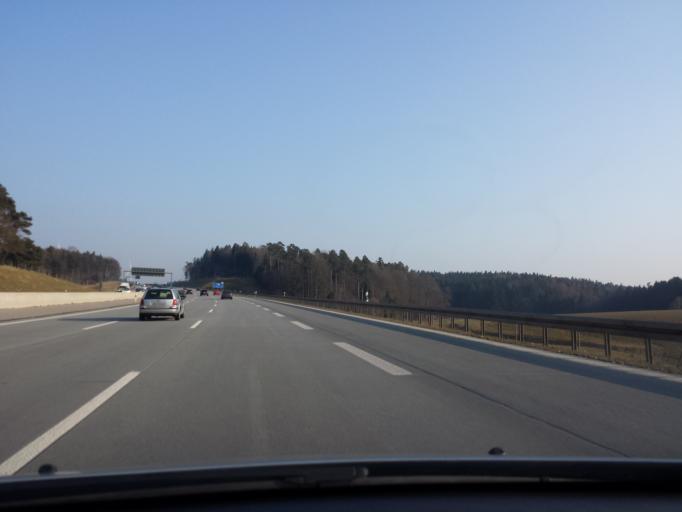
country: DE
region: Bavaria
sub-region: Swabia
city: Adelzhausen
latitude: 48.3487
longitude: 11.1383
